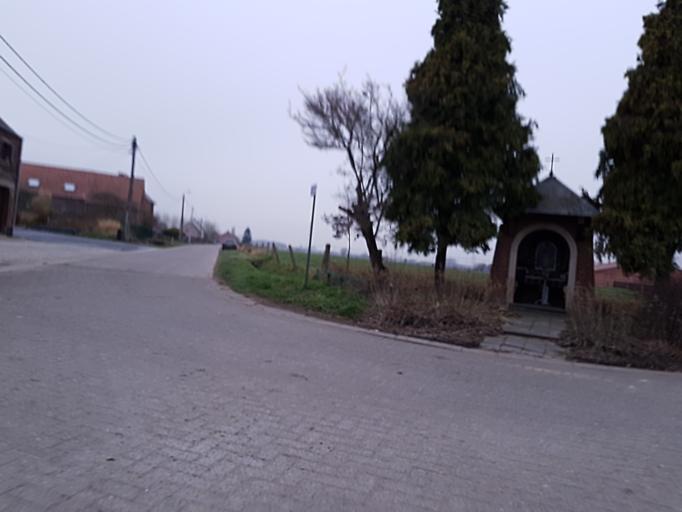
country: BE
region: Flanders
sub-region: Provincie Vlaams-Brabant
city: Kapelle-op-den-Bos
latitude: 51.0264
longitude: 4.4105
